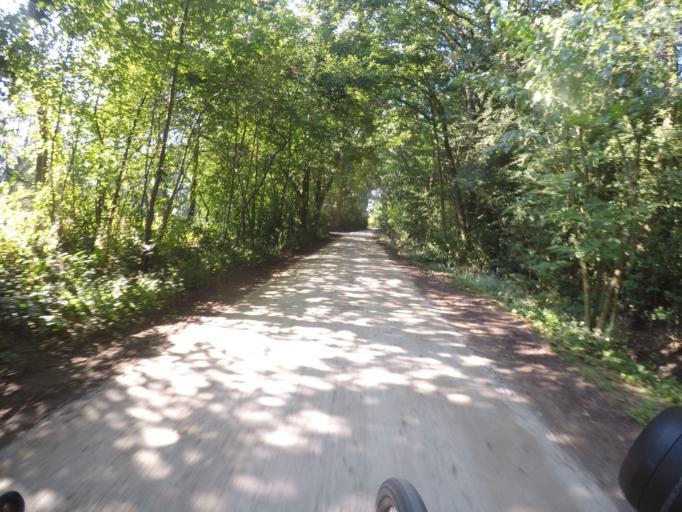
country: DE
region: Schleswig-Holstein
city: Oststeinbek
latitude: 53.5405
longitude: 10.1522
